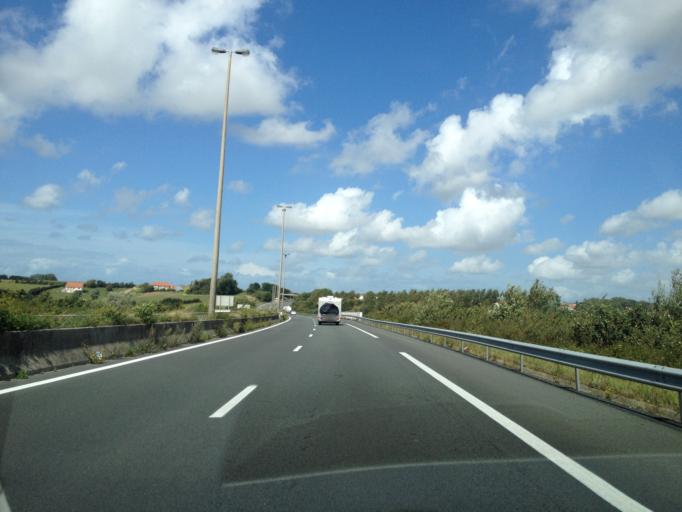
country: FR
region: Nord-Pas-de-Calais
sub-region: Departement du Pas-de-Calais
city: Marquise
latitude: 50.8091
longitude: 1.6943
